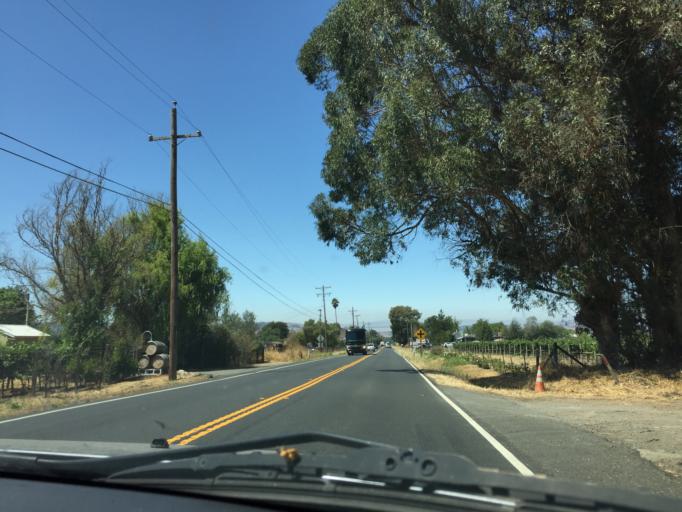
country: US
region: California
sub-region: Sonoma County
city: Sonoma
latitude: 38.2467
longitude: -122.4148
